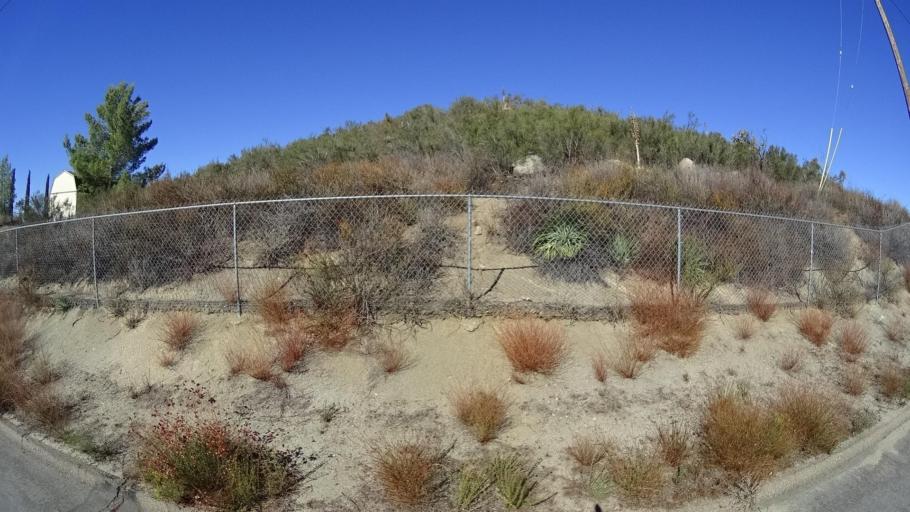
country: US
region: California
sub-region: San Diego County
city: Alpine
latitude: 32.8329
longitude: -116.7006
